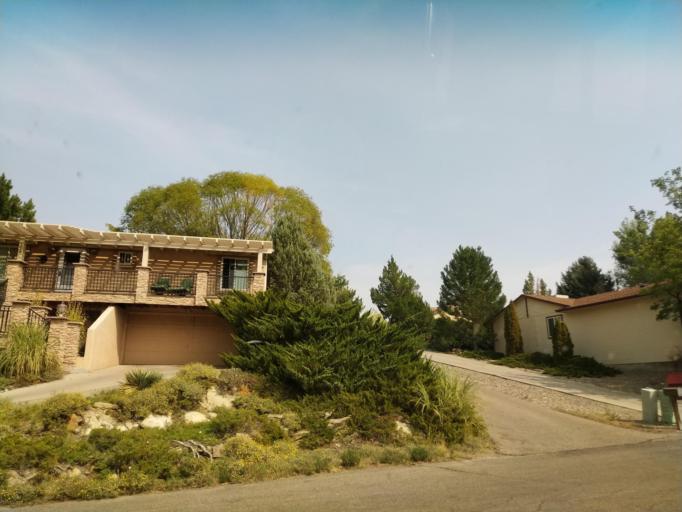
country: US
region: Colorado
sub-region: Mesa County
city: Redlands
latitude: 39.0620
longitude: -108.6133
